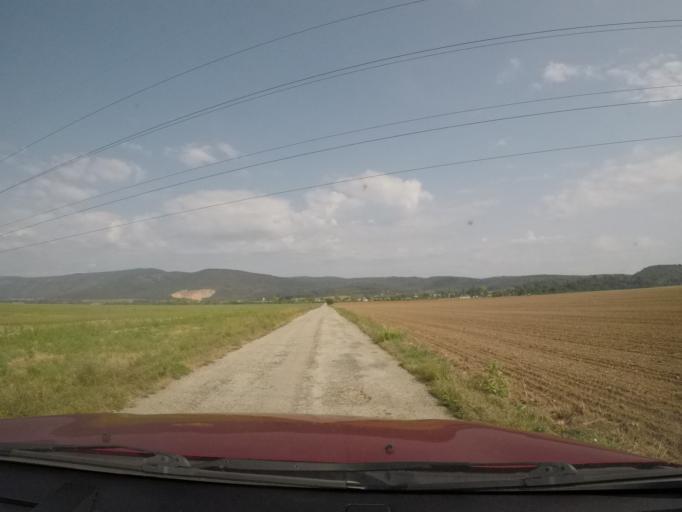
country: SK
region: Kosicky
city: Moldava nad Bodvou
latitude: 48.5976
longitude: 20.9550
